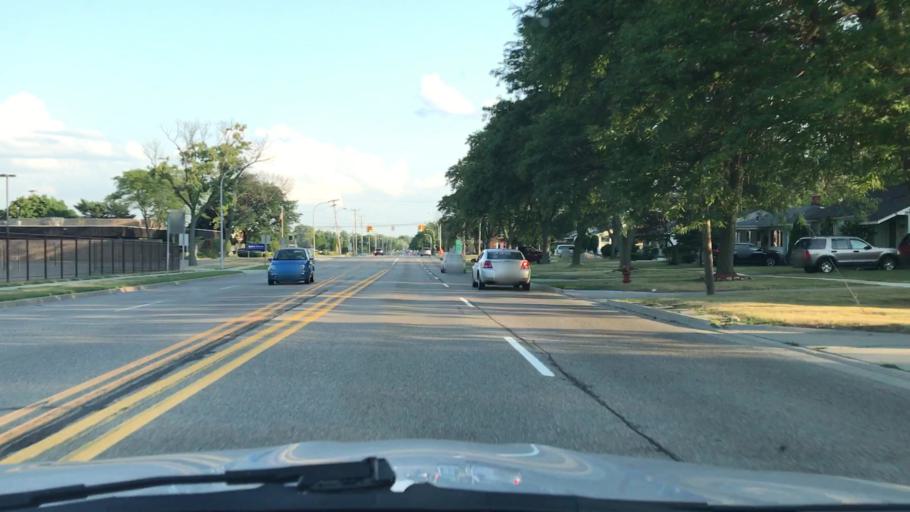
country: US
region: Michigan
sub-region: Oakland County
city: Clawson
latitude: 42.5270
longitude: -83.1653
